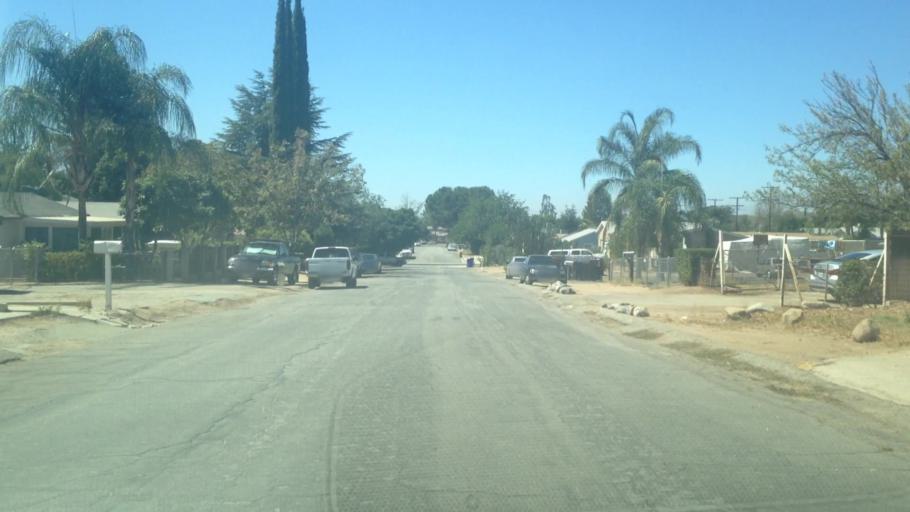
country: US
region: California
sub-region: San Bernardino County
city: Yucaipa
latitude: 34.0308
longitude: -117.0394
